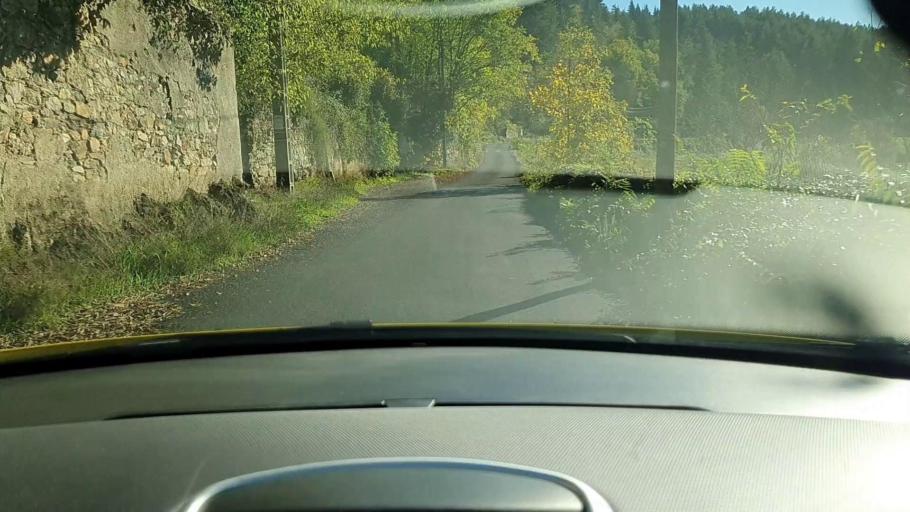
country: FR
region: Languedoc-Roussillon
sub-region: Departement du Gard
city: Le Vigan
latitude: 43.9872
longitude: 3.6082
